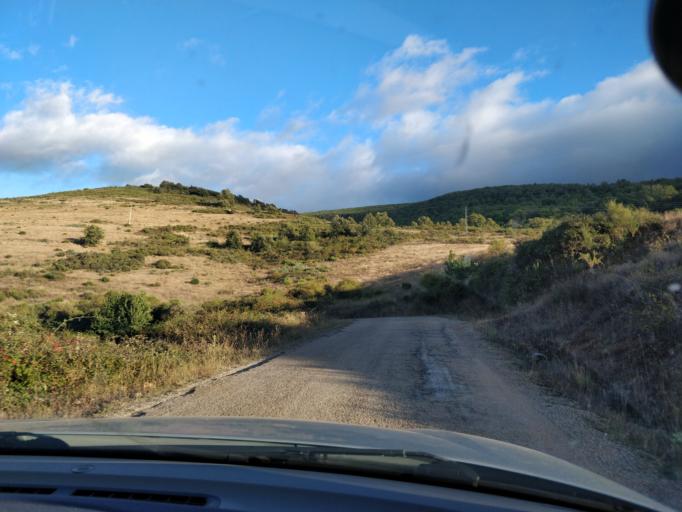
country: ES
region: Castille and Leon
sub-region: Provincia de Leon
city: Borrenes
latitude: 42.4856
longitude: -6.7011
